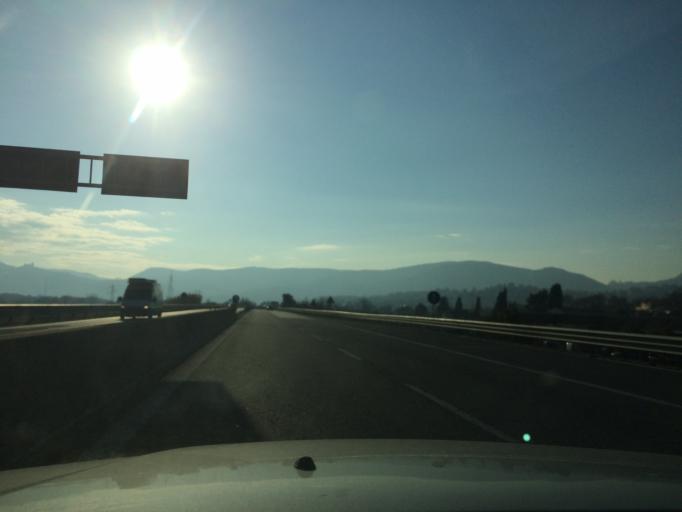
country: IT
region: Umbria
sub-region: Provincia di Terni
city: Narni Scalo
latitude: 42.5555
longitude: 12.5349
